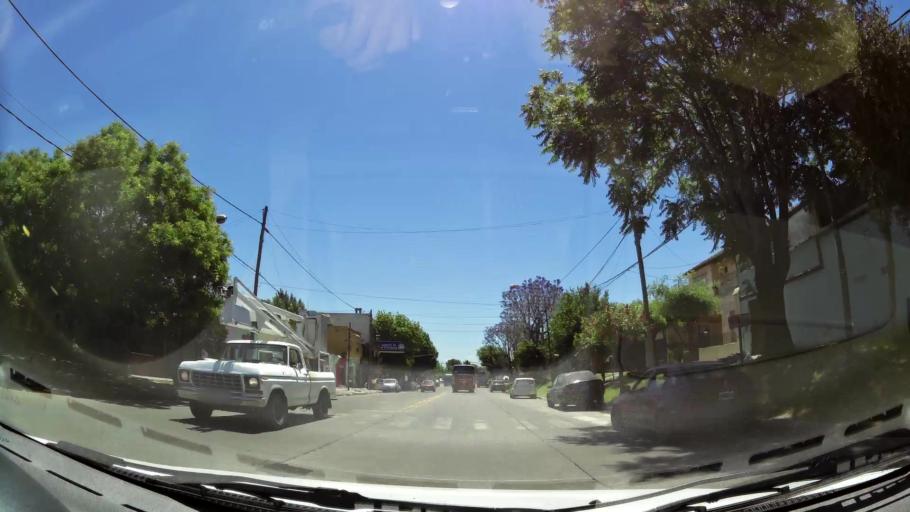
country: AR
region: Buenos Aires
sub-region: Partido de Tigre
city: Tigre
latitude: -34.5044
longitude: -58.5838
